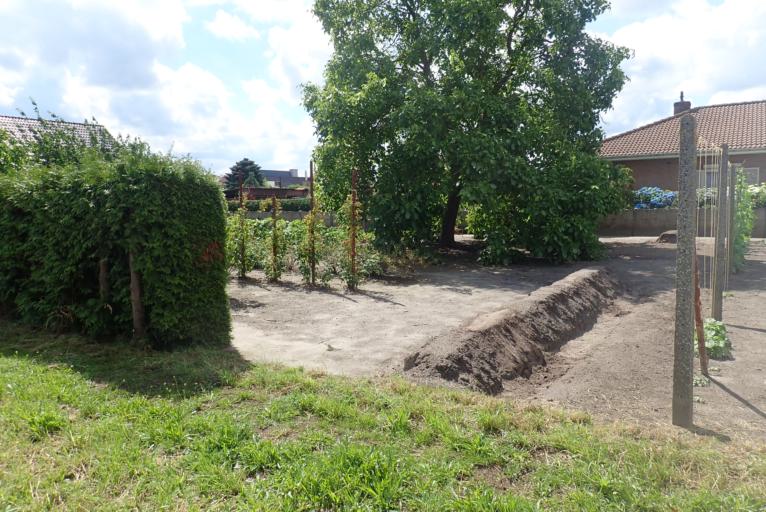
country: BE
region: Flanders
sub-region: Provincie Antwerpen
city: Oostmalle
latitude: 51.3063
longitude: 4.7327
